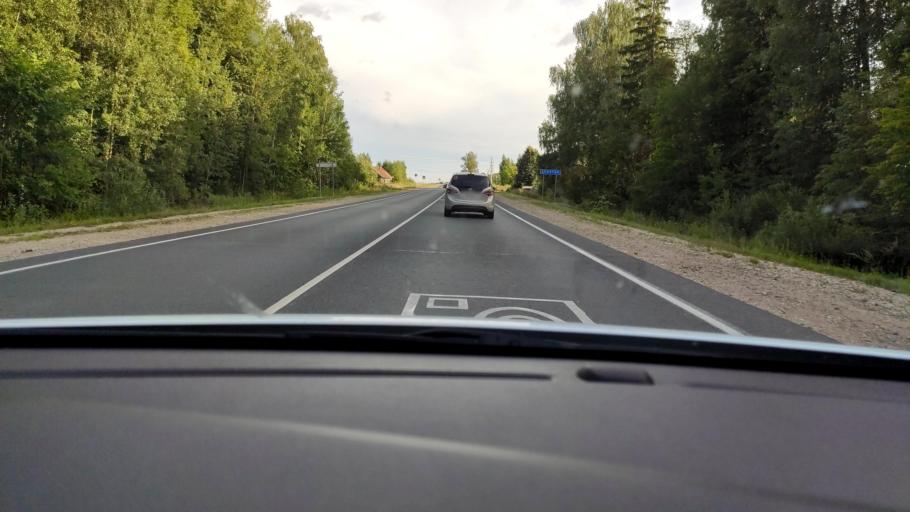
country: RU
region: Mariy-El
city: Suslonger
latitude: 56.2265
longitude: 48.2342
